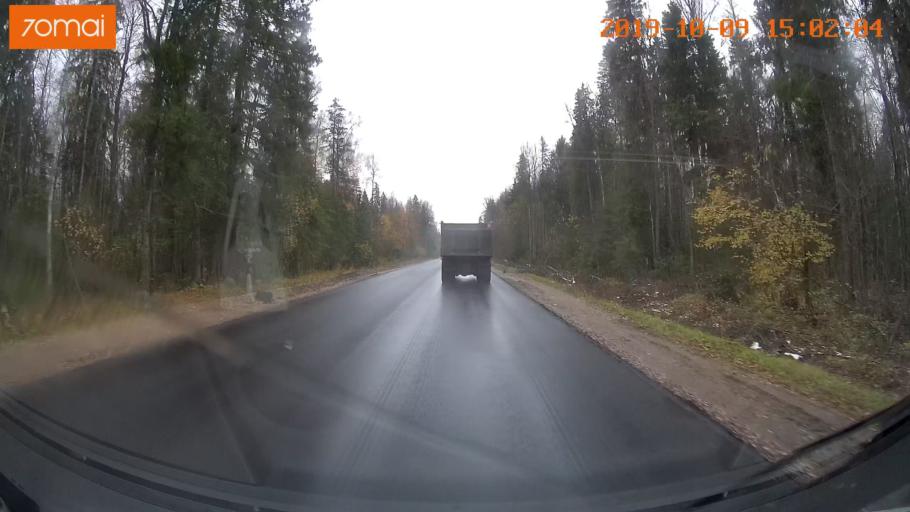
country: RU
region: Kostroma
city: Chistyye Bory
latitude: 58.2899
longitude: 41.6804
